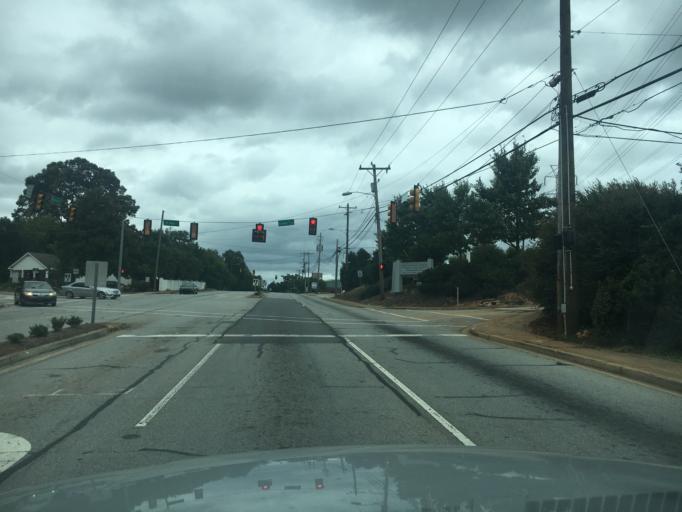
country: US
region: South Carolina
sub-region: Greenville County
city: Greenville
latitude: 34.8807
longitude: -82.3877
